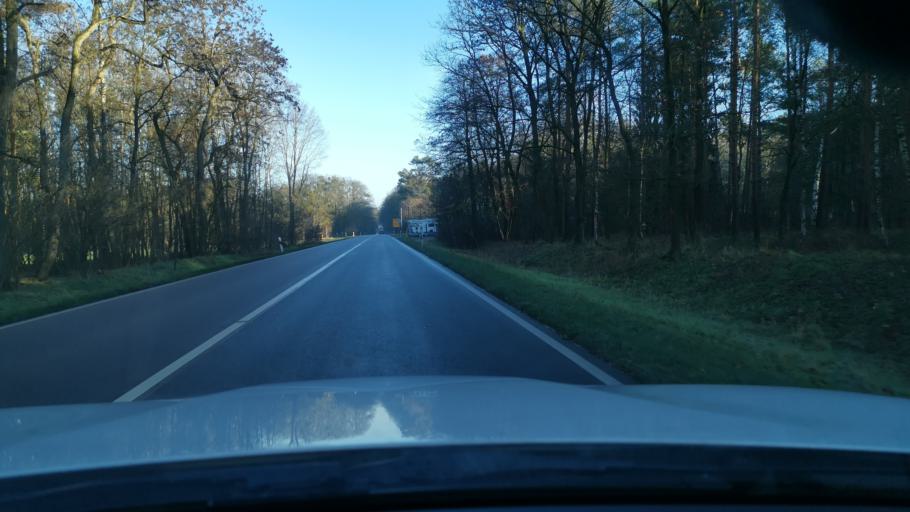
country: DE
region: Saxony-Anhalt
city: Abtsdorf
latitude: 51.9304
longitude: 12.7088
